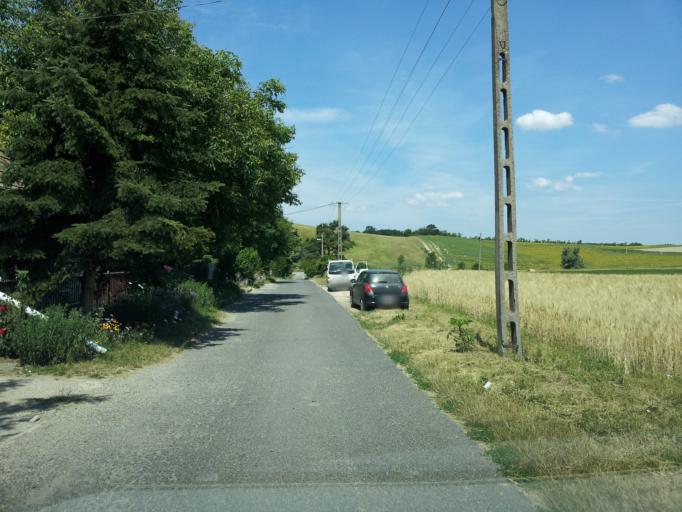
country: HU
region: Fejer
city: Many
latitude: 47.5569
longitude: 18.5929
